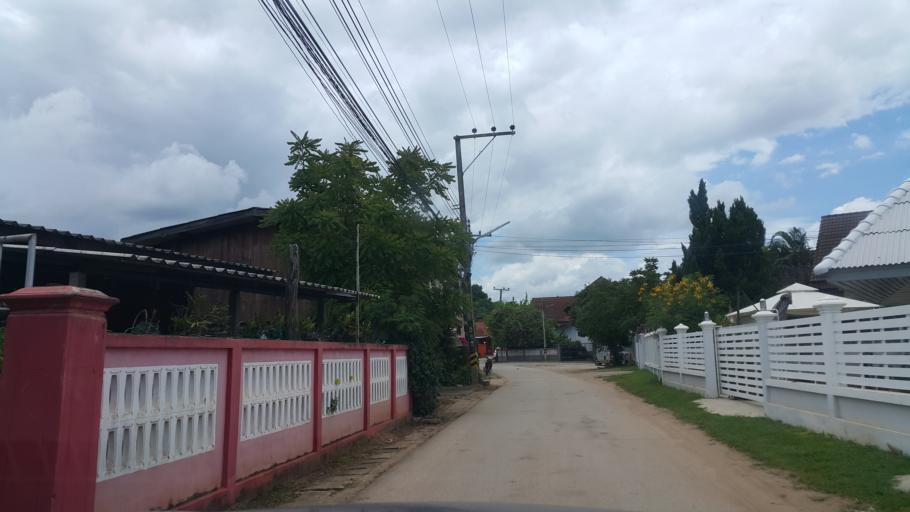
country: TH
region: Chiang Mai
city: Mae Taeng
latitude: 19.1517
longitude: 98.9809
